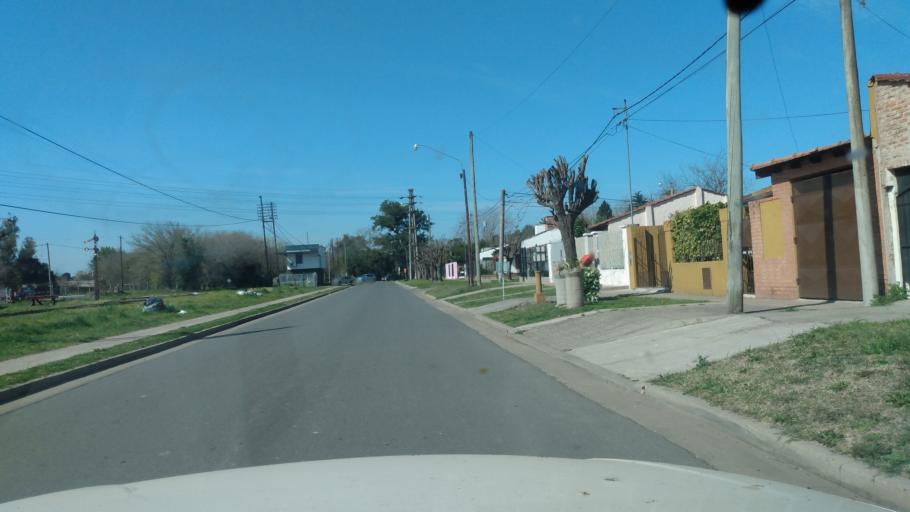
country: AR
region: Buenos Aires
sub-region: Partido de Lujan
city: Lujan
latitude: -34.5766
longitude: -59.1009
